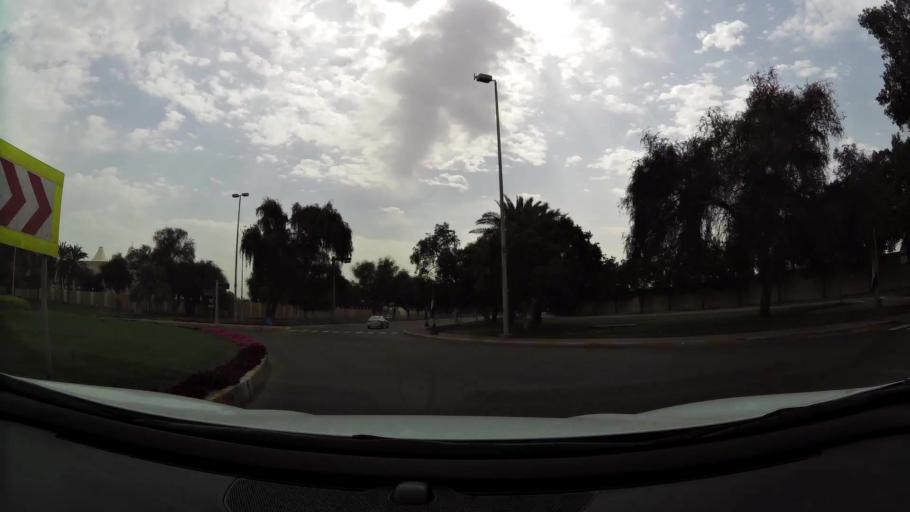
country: AE
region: Abu Dhabi
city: Abu Dhabi
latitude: 24.4498
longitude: 54.3724
